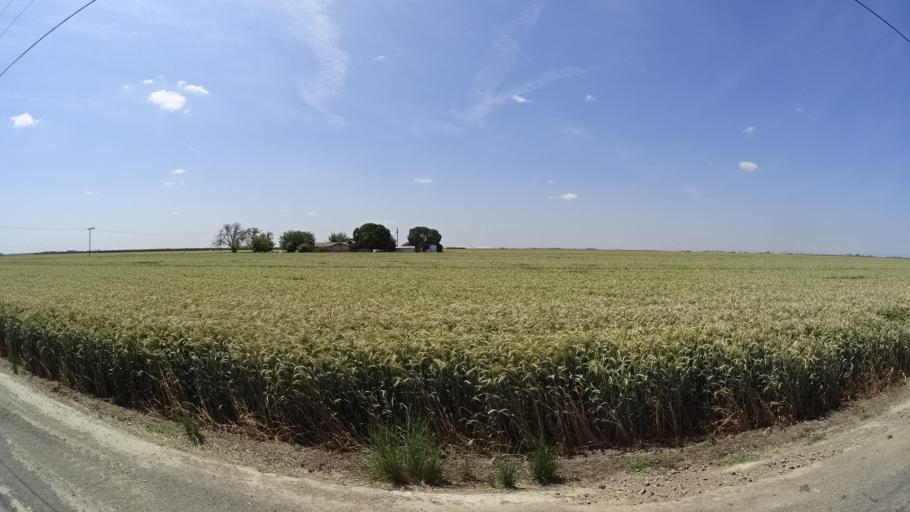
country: US
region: California
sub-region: Tulare County
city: Goshen
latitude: 36.2691
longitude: -119.5116
